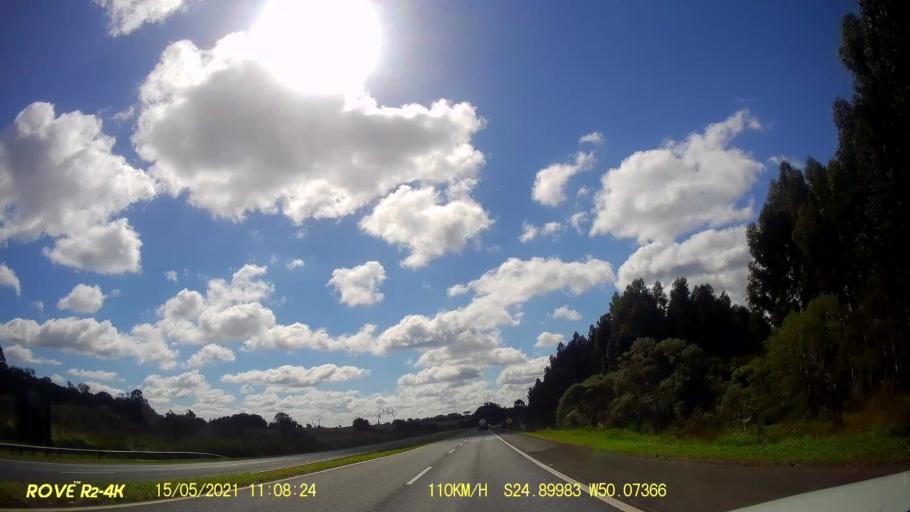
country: BR
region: Parana
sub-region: Carambei
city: Carambei
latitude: -24.9004
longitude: -50.0742
